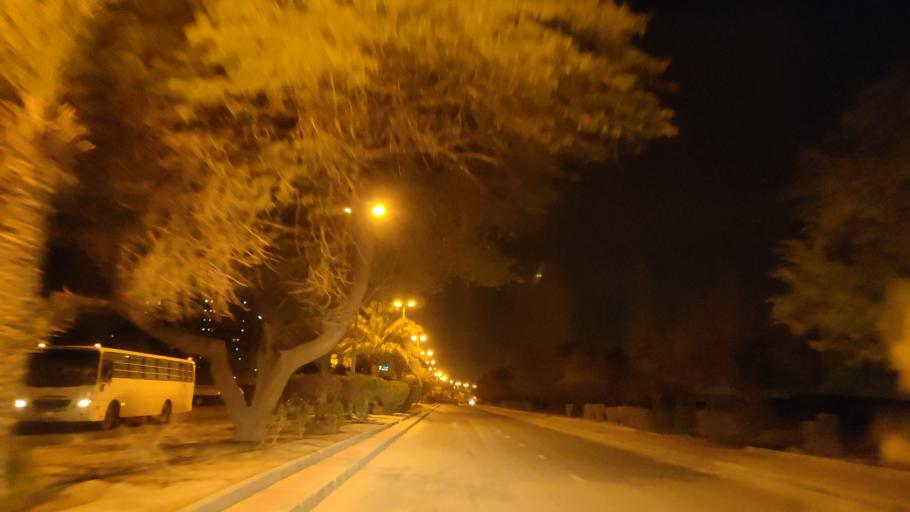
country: KW
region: Al Farwaniyah
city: Al Farwaniyah
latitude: 29.2554
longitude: 47.9458
